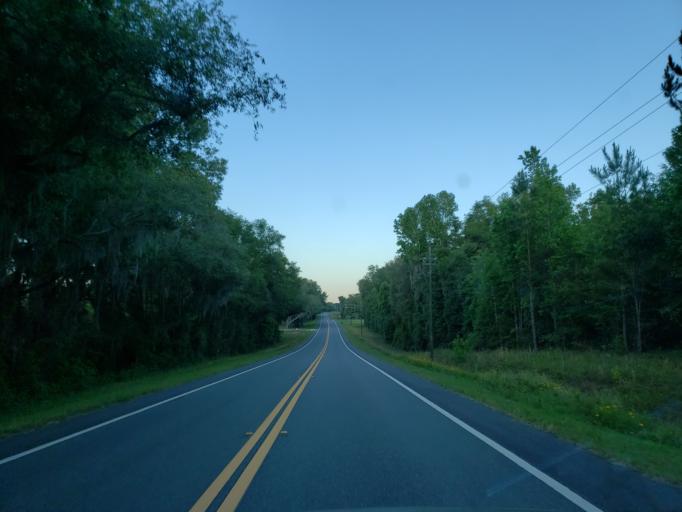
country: US
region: Florida
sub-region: Madison County
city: Madison
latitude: 30.5813
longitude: -83.2182
